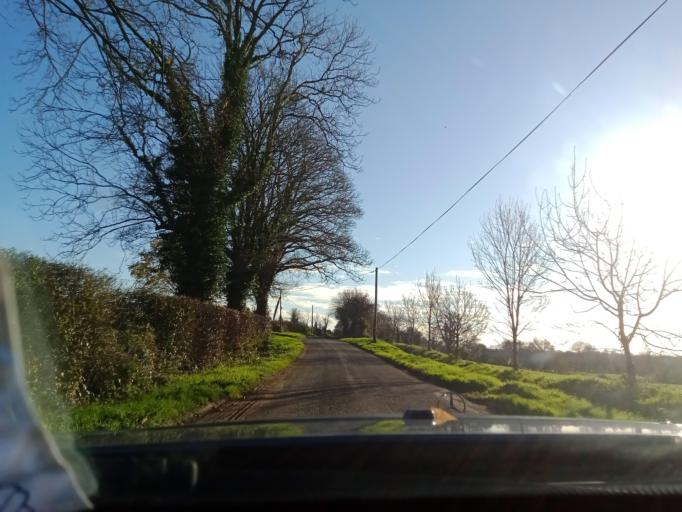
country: IE
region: Leinster
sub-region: Kilkenny
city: Mooncoin
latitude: 52.3379
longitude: -7.2657
